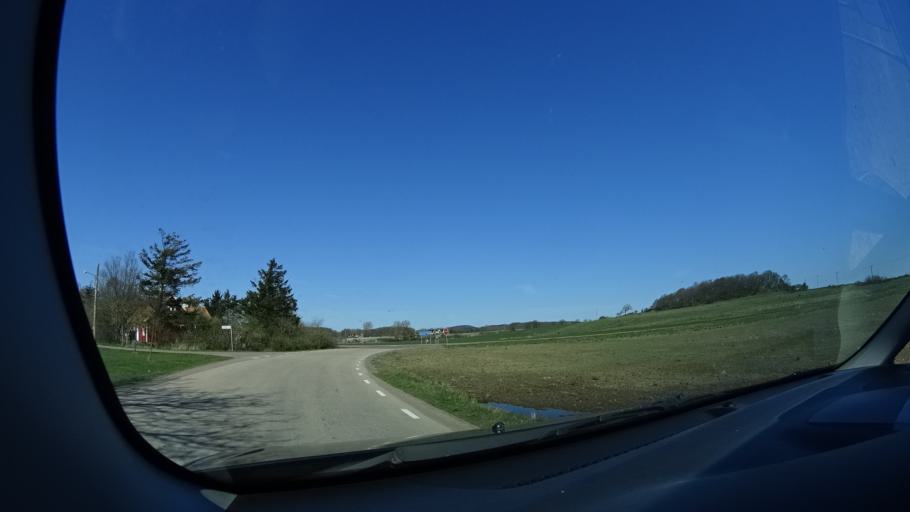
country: SE
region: Skane
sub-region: Hoganas Kommun
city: Hoganas
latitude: 56.2493
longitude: 12.5648
